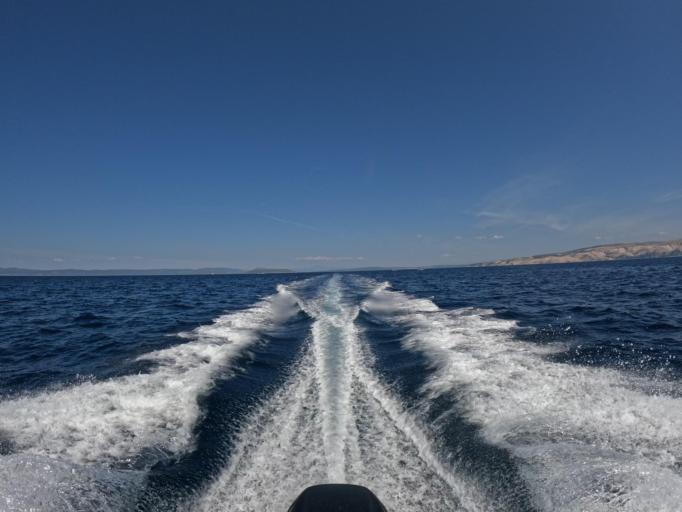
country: HR
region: Primorsko-Goranska
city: Lopar
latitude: 44.8936
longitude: 14.6422
